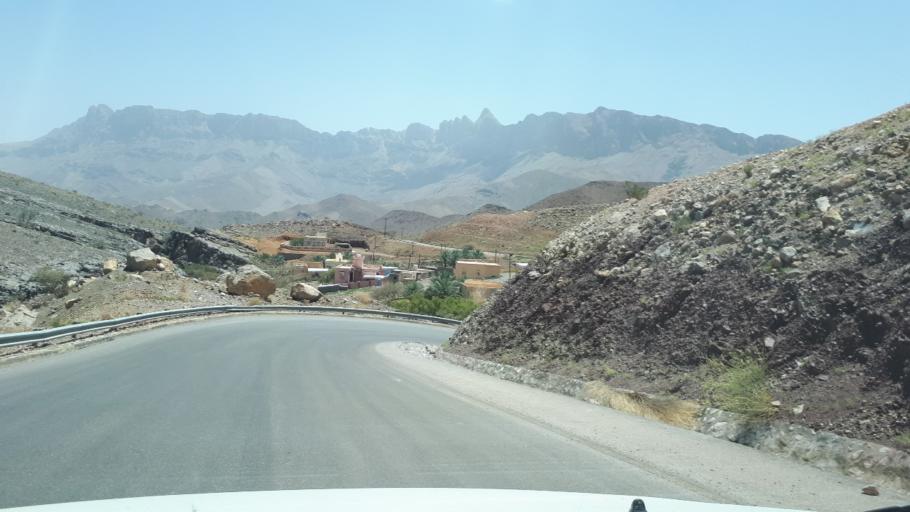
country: OM
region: Muhafazat ad Dakhiliyah
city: Bahla'
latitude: 23.1939
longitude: 57.1371
